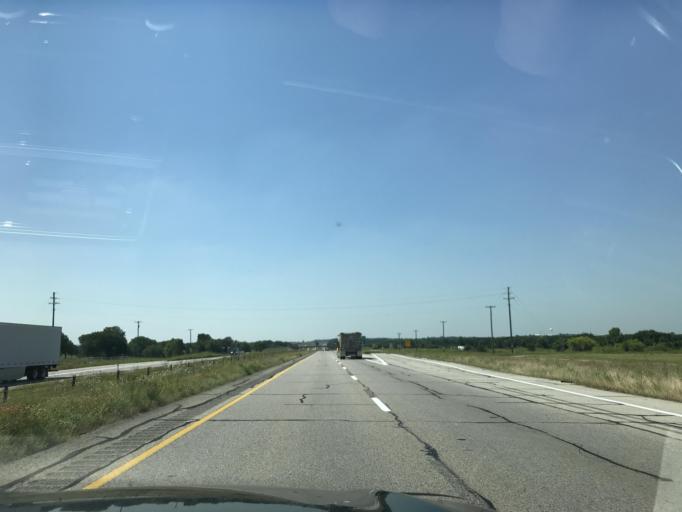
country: US
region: Texas
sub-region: Johnson County
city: Grandview
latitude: 32.3050
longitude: -97.1820
